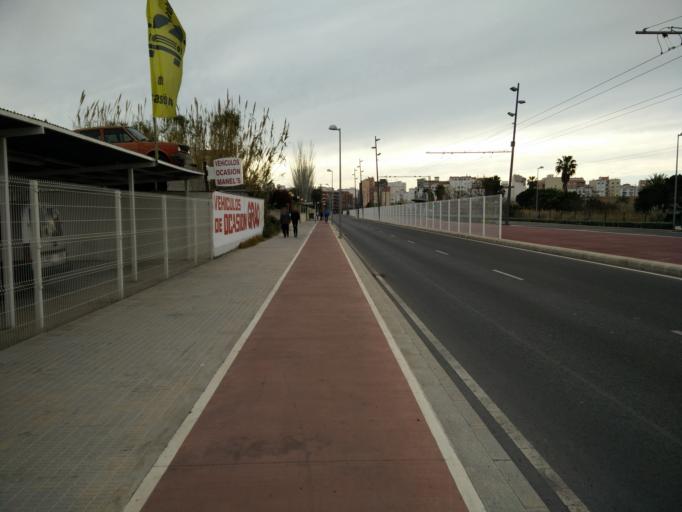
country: ES
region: Valencia
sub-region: Provincia de Castello
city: Castello de la Plana
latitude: 39.9775
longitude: 0.0069
